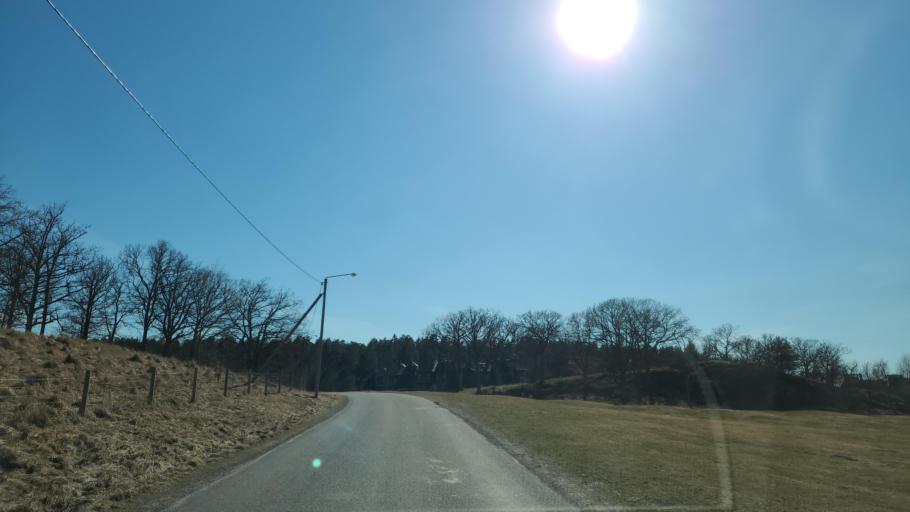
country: SE
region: Stockholm
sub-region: Varmdo Kommun
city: Hemmesta
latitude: 59.2768
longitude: 18.5485
